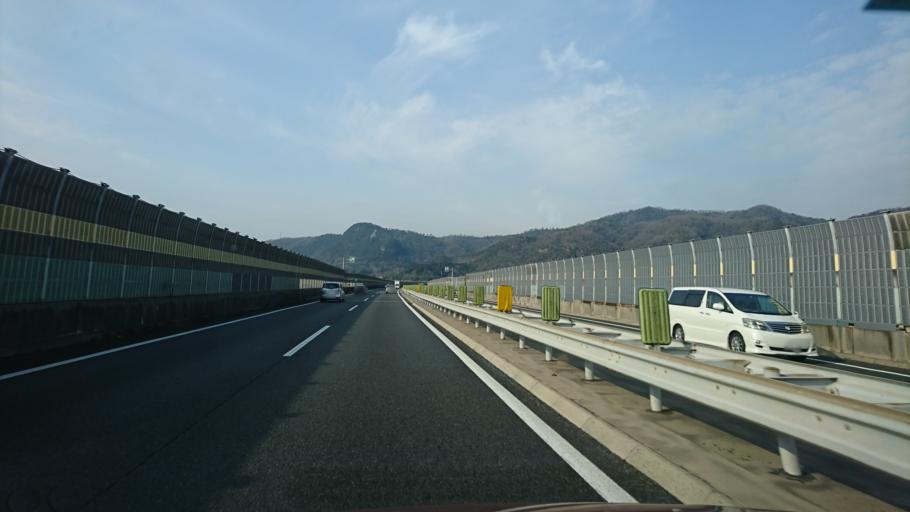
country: JP
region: Okayama
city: Okayama-shi
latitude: 34.7374
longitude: 134.0077
